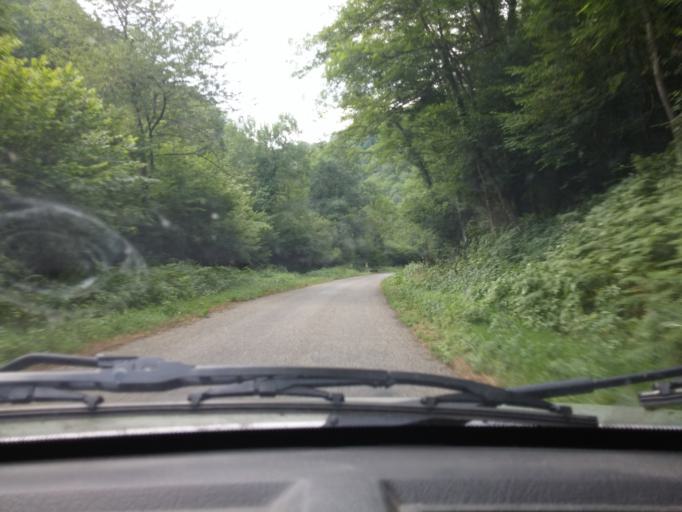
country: FR
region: Midi-Pyrenees
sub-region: Departement de l'Ariege
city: Saint-Girons
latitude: 42.9131
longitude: 1.2062
